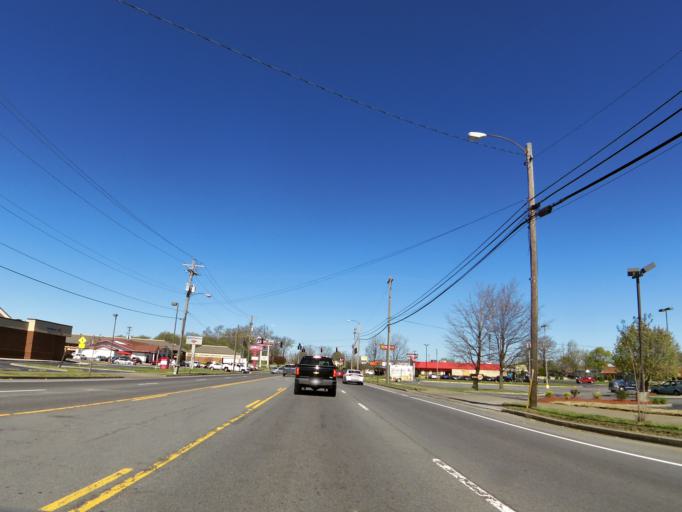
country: US
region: Tennessee
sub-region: Robertson County
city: Springfield
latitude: 36.4944
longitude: -86.8781
